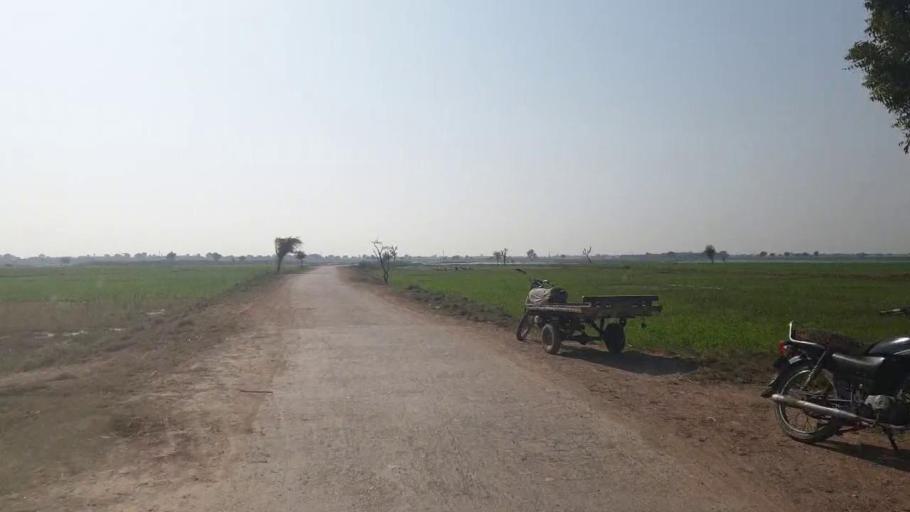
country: PK
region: Sindh
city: Tando Adam
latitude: 25.7483
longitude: 68.6140
